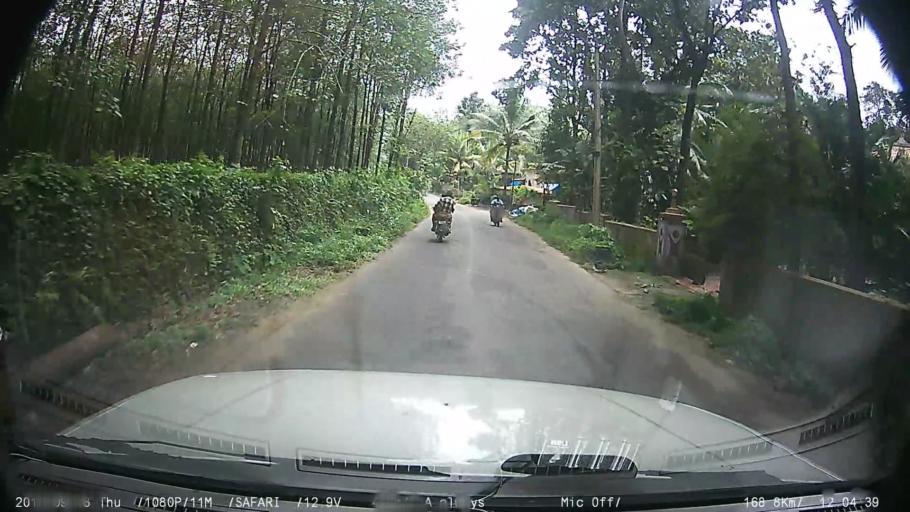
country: IN
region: Kerala
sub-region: Ernakulam
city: Kotamangalam
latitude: 10.1061
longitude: 76.6785
